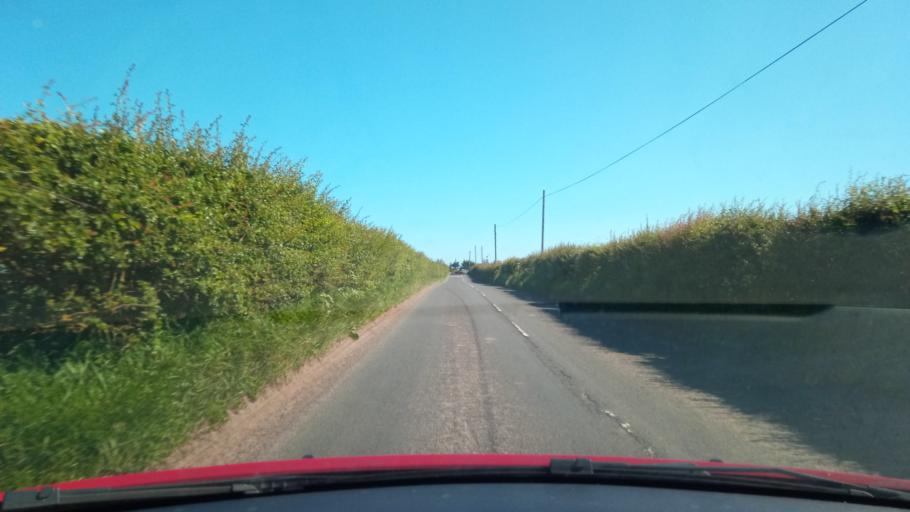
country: GB
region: Scotland
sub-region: East Lothian
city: East Linton
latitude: 56.0396
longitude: -2.6428
